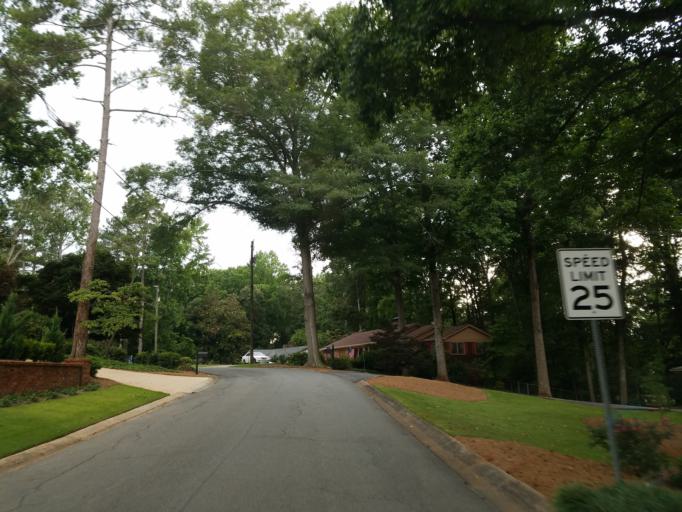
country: US
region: Georgia
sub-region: Cobb County
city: Marietta
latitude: 33.9446
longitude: -84.5668
